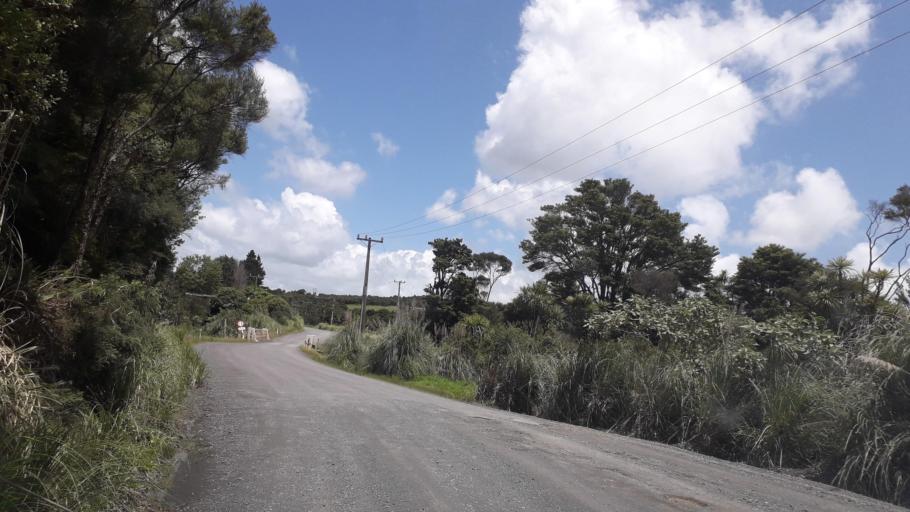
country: NZ
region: Northland
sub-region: Far North District
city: Taipa
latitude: -35.0131
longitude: 173.4200
